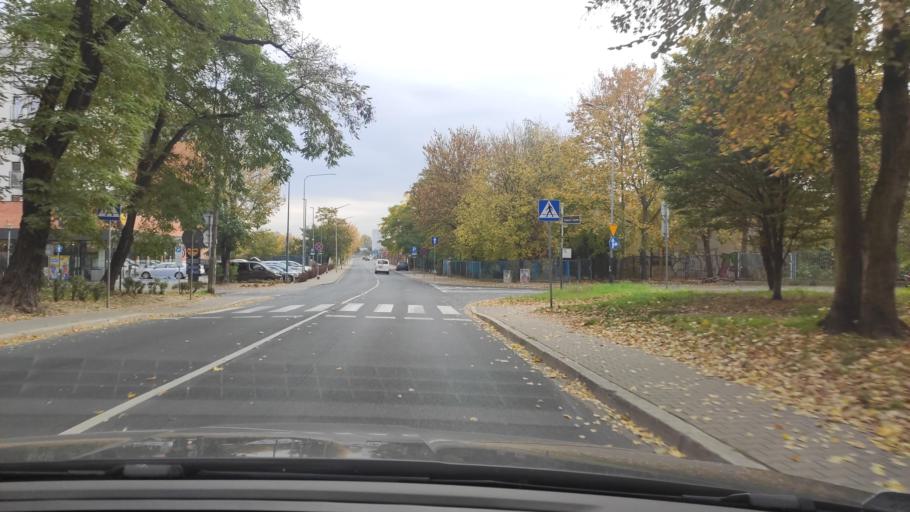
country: PL
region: Greater Poland Voivodeship
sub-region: Poznan
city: Poznan
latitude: 52.4151
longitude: 16.9333
